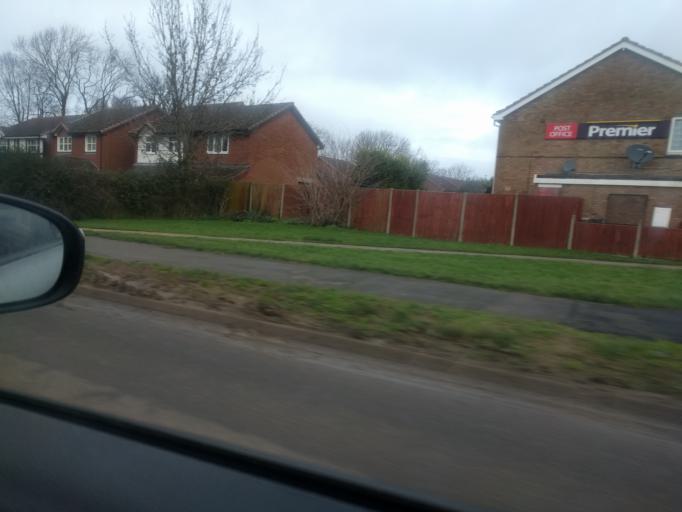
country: GB
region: England
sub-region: Gloucestershire
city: Mickleton
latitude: 52.1224
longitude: -1.7408
